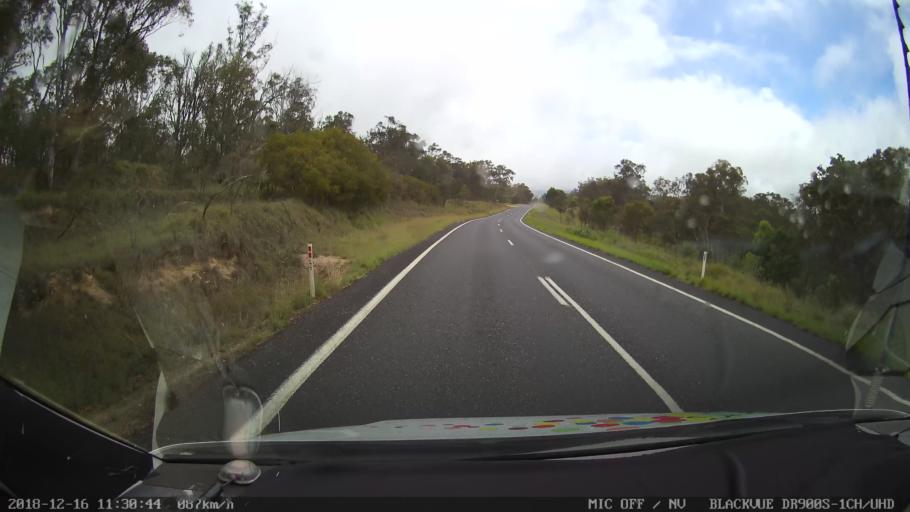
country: AU
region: New South Wales
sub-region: Tenterfield Municipality
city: Carrolls Creek
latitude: -29.0288
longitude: 152.1218
